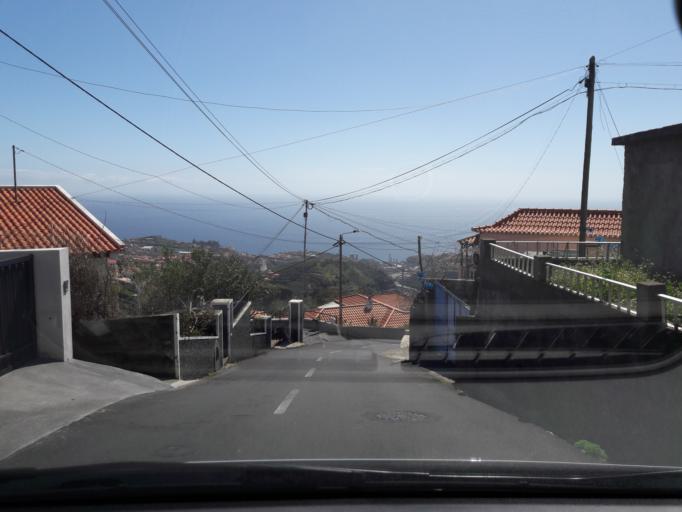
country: PT
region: Madeira
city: Camara de Lobos
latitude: 32.6699
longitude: -16.9548
